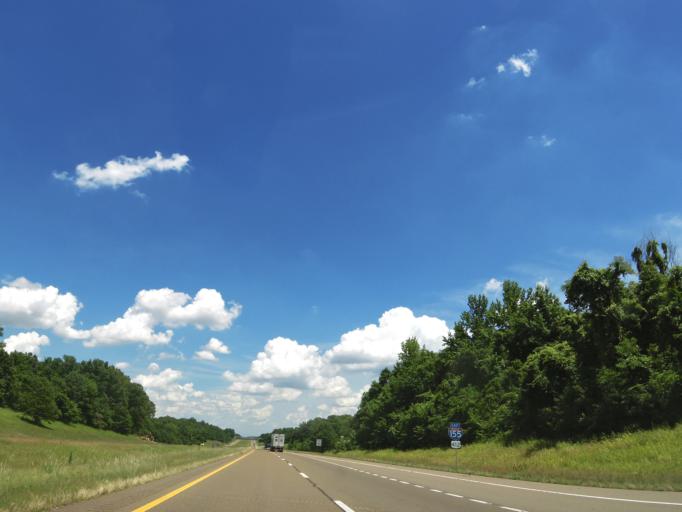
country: US
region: Tennessee
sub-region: Dyer County
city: Dyersburg
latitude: 36.0738
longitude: -89.4831
